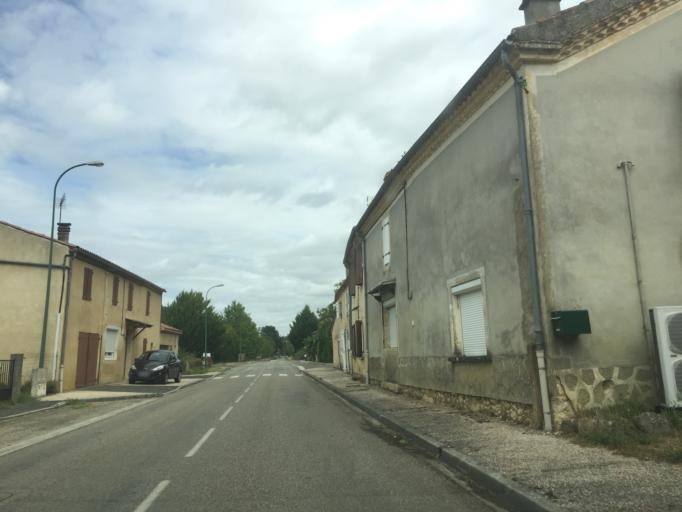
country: FR
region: Midi-Pyrenees
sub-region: Departement du Gers
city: Vic-Fezensac
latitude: 43.6496
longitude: 0.3433
